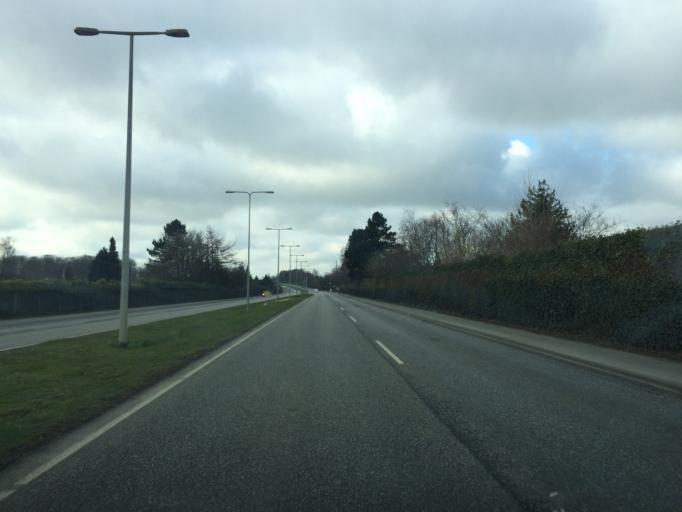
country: DK
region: South Denmark
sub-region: Fredericia Kommune
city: Snoghoj
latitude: 55.5460
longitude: 9.7216
